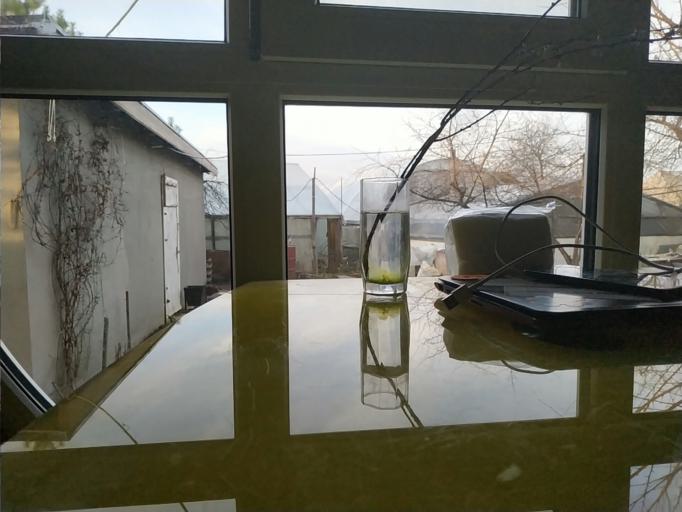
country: RU
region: Republic of Karelia
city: Suoyarvi
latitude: 62.2637
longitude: 32.0892
